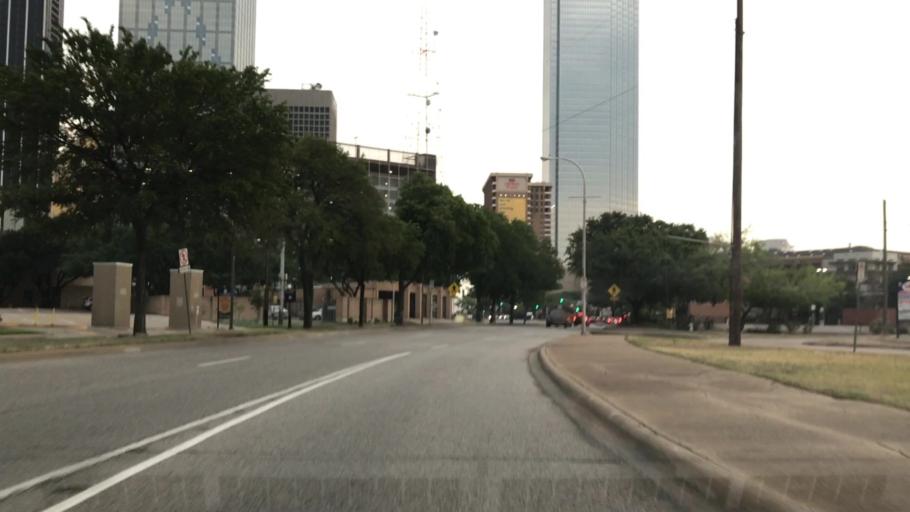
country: US
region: Texas
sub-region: Dallas County
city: Dallas
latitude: 32.7850
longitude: -96.8041
